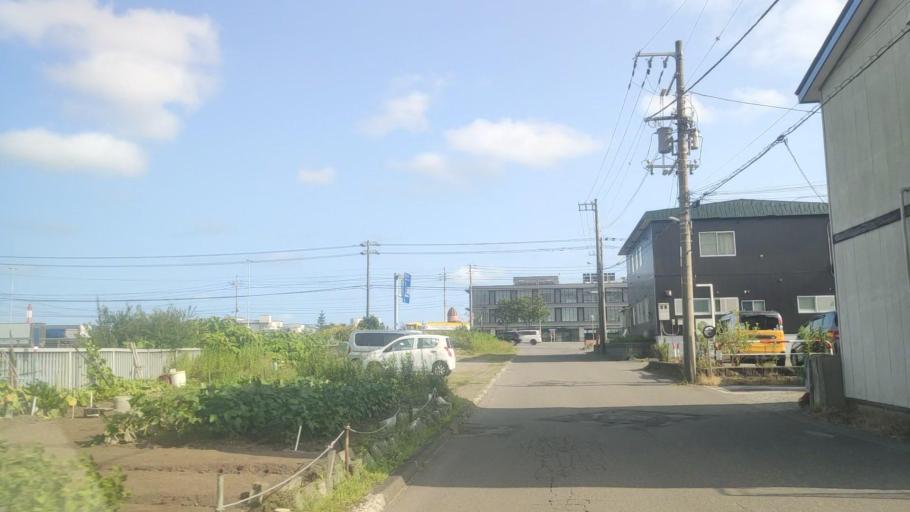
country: JP
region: Hokkaido
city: Tomakomai
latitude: 42.6485
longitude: 141.6292
